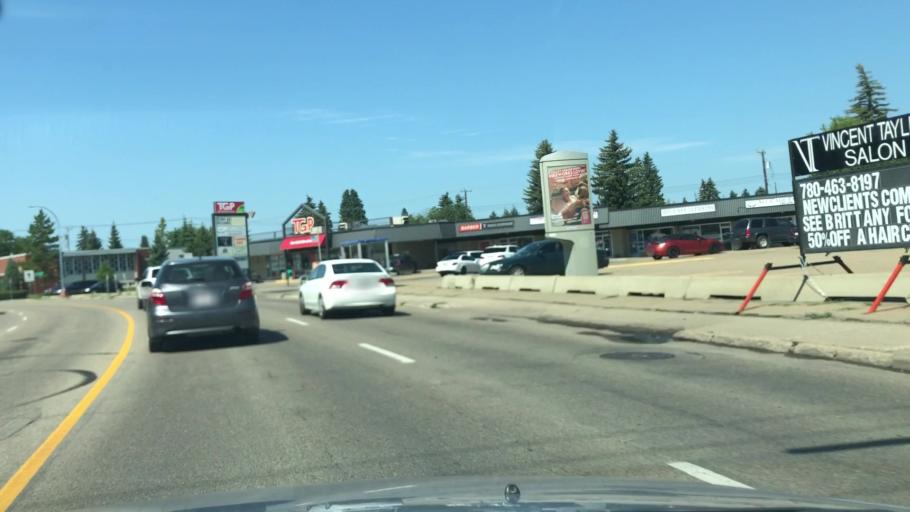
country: CA
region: Alberta
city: Edmonton
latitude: 53.5514
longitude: -113.4187
